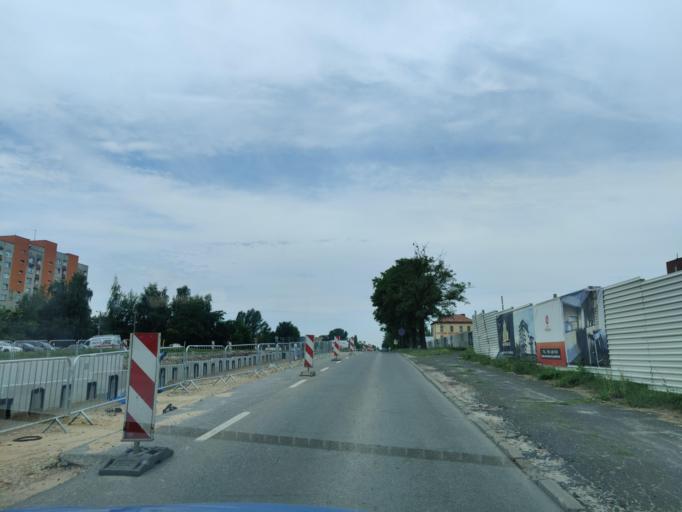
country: PL
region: Silesian Voivodeship
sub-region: Dabrowa Gornicza
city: Dabrowa Gornicza
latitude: 50.2830
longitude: 19.1883
